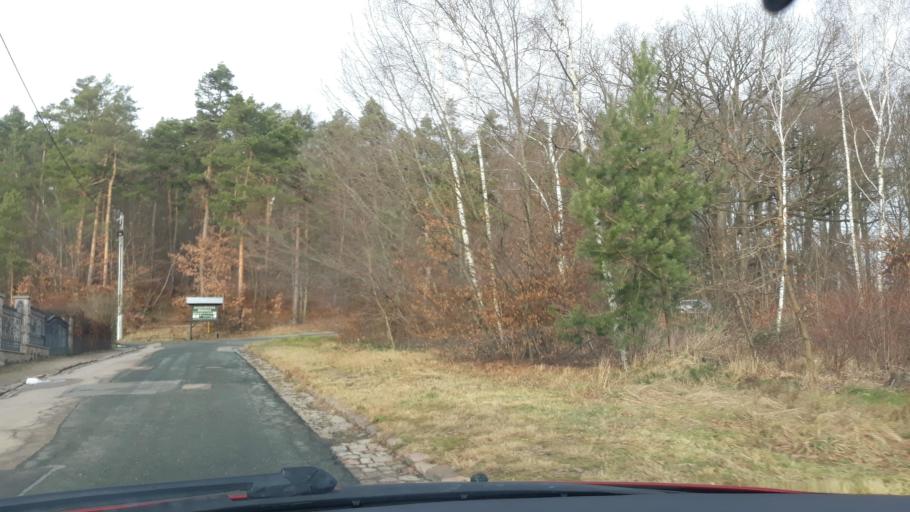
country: DE
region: Saxony
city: Kirchberg
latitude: 50.6235
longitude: 12.5143
